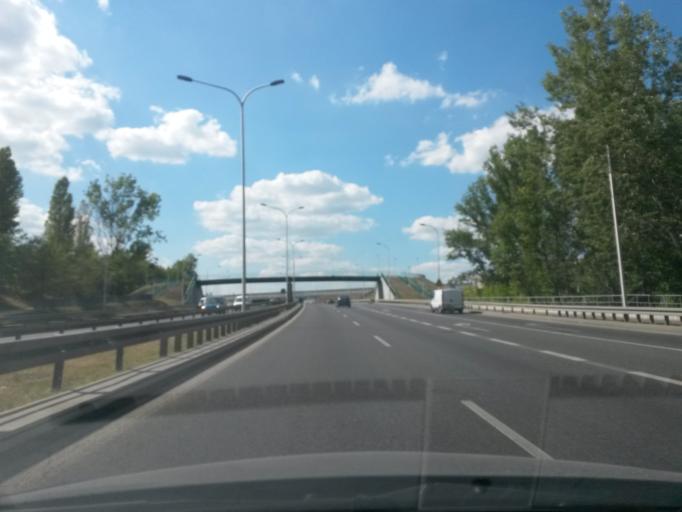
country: PL
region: Masovian Voivodeship
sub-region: Warszawa
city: Bielany
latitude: 52.3018
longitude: 20.9486
